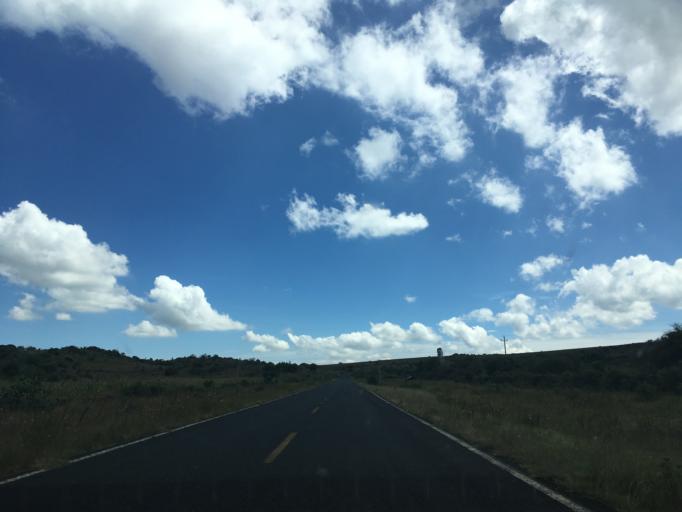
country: MX
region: Michoacan
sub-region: Morelia
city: Cuto de la Esperanza
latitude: 19.7727
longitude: -101.3870
